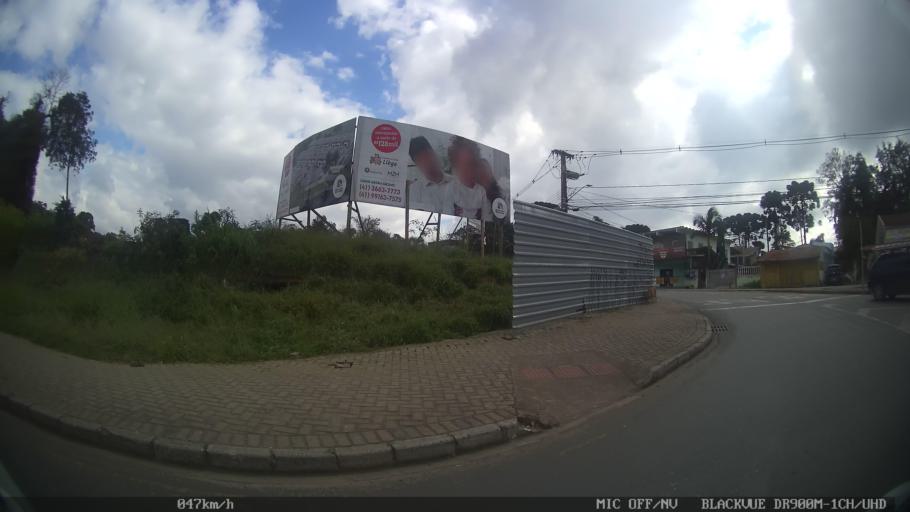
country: BR
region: Parana
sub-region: Colombo
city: Colombo
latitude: -25.3486
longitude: -49.2019
